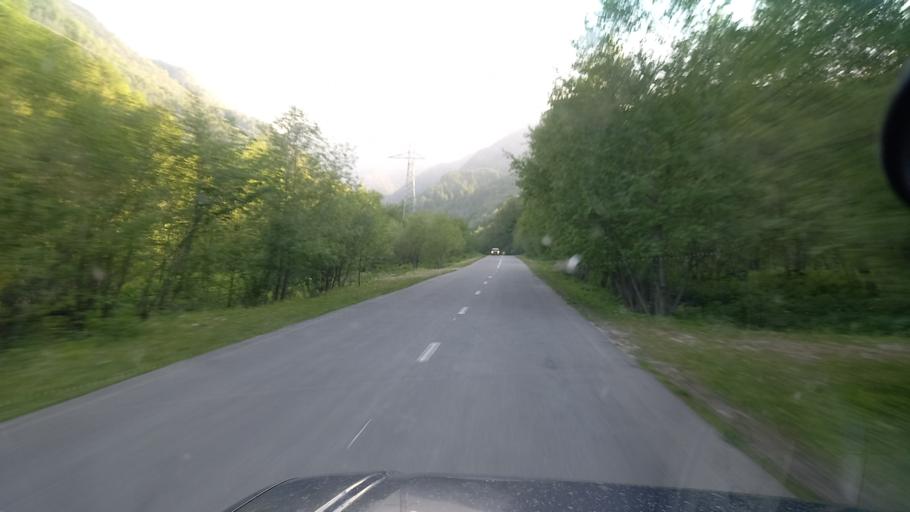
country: RU
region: North Ossetia
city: Tarskoye
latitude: 42.9047
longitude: 44.9559
